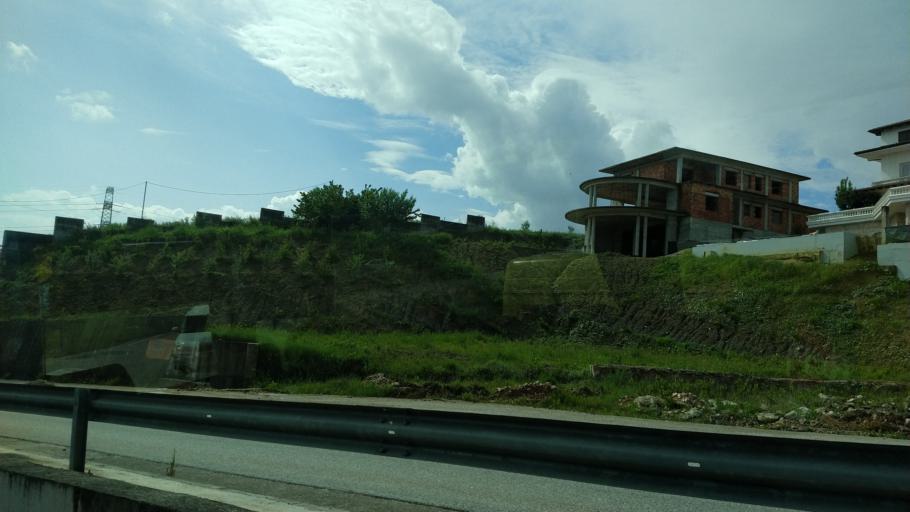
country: AL
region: Tirane
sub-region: Rrethi i Tiranes
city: Kashar
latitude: 41.3655
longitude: 19.7053
